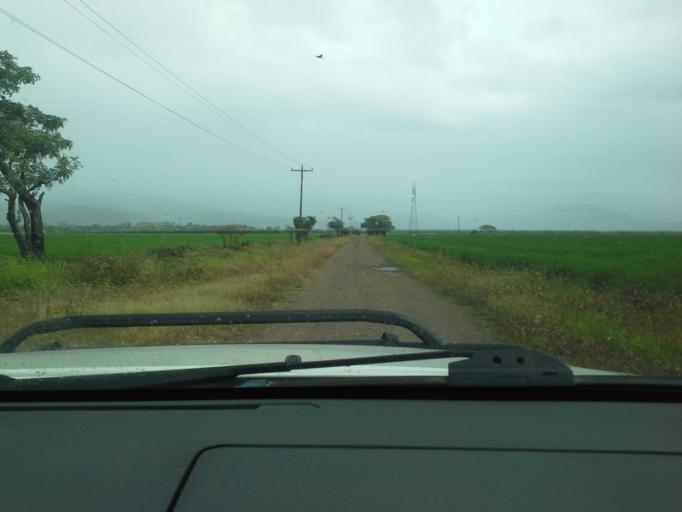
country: NI
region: Matagalpa
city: Ciudad Dario
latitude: 12.8432
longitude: -86.1737
